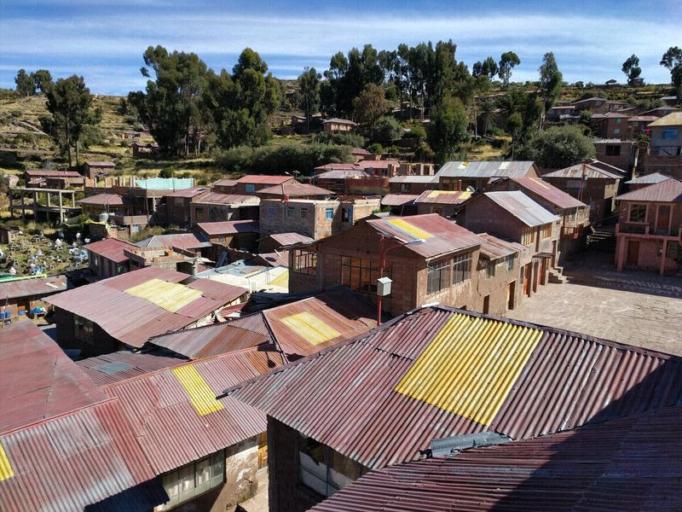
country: PE
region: Puno
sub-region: Provincia de Puno
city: Taquile
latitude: -15.7646
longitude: -69.6844
